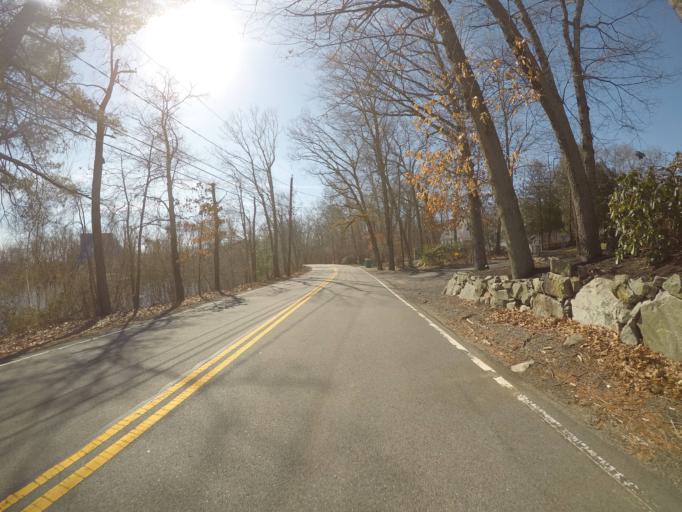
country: US
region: Massachusetts
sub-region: Norfolk County
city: Stoughton
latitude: 42.0783
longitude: -71.1170
